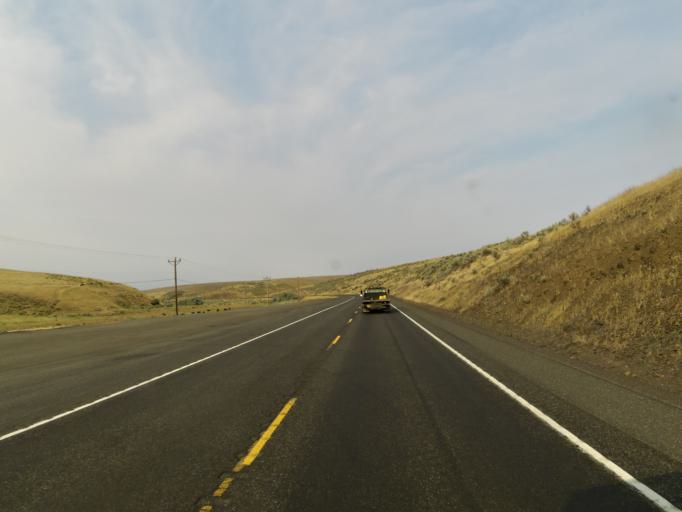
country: US
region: Oregon
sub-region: Sherman County
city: Moro
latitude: 45.5036
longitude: -120.6991
